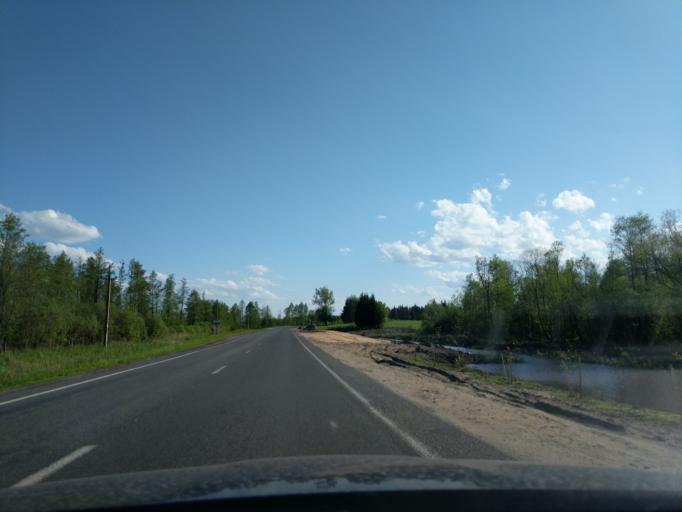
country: BY
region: Minsk
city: Myadzyel
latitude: 54.8634
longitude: 26.9330
